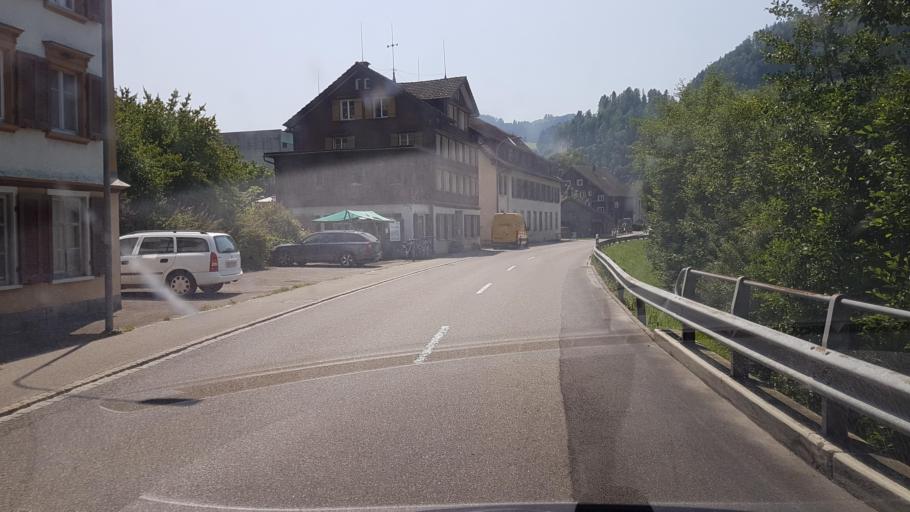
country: CH
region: Saint Gallen
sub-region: Wahlkreis Toggenburg
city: Mogelsberg
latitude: 47.3471
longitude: 9.1312
